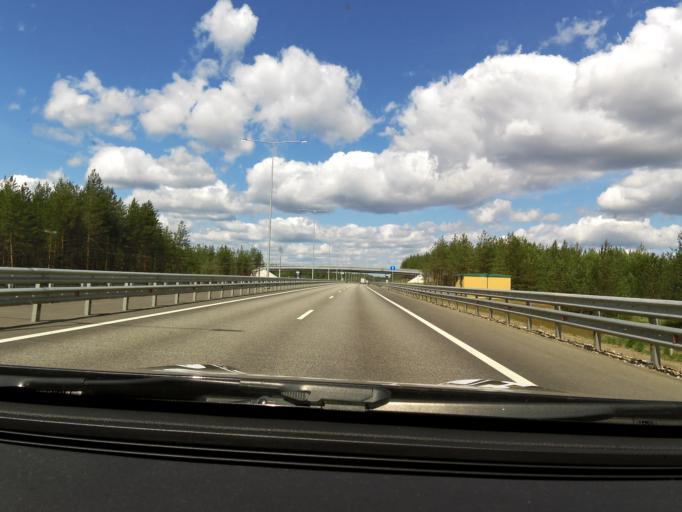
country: RU
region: Tverskaya
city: Krasnomayskiy
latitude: 57.4884
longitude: 34.3140
